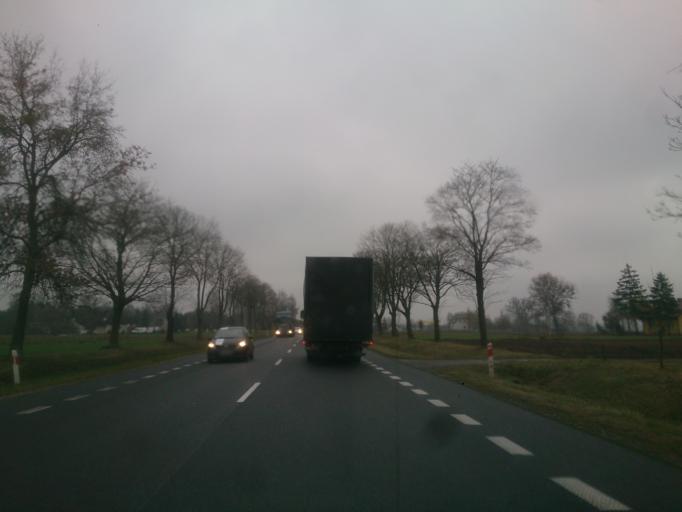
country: PL
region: Masovian Voivodeship
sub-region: Powiat sierpecki
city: Zawidz
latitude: 52.8006
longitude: 19.8558
